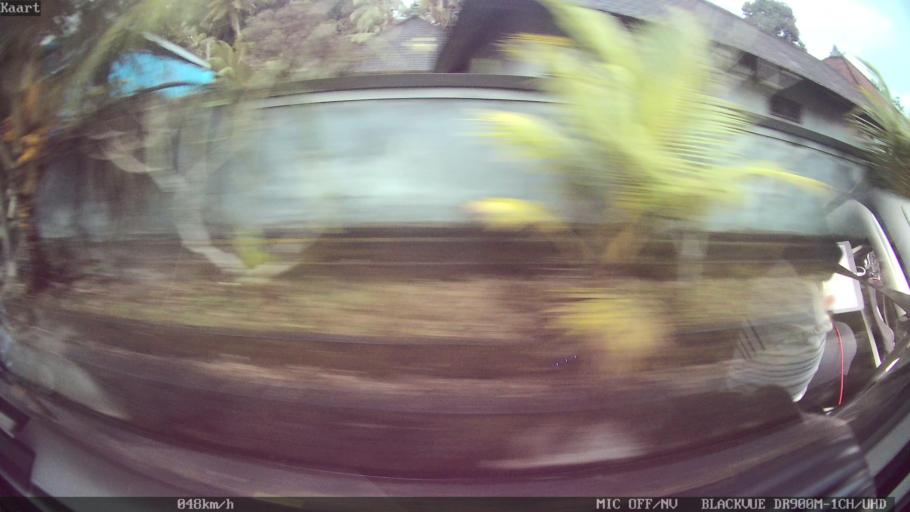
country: ID
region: Bali
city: Banjar Teguan
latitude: -8.4980
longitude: 115.2376
